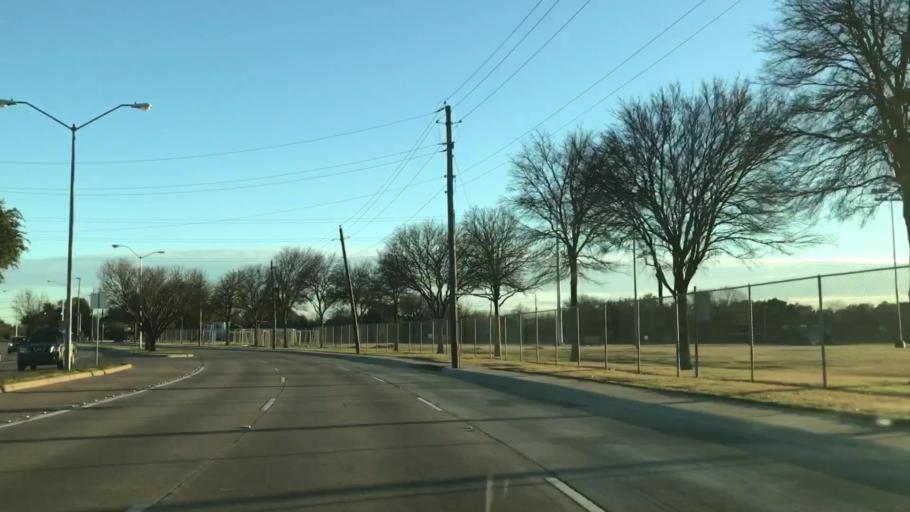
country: US
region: Texas
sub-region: Dallas County
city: Addison
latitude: 32.9783
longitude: -96.7858
